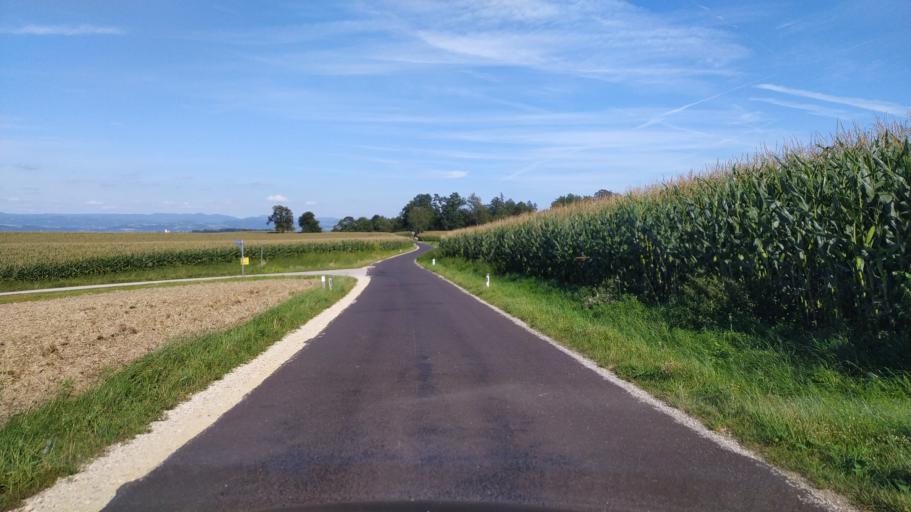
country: AT
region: Lower Austria
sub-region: Politischer Bezirk Amstetten
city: Strengberg
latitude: 48.1190
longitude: 14.6422
